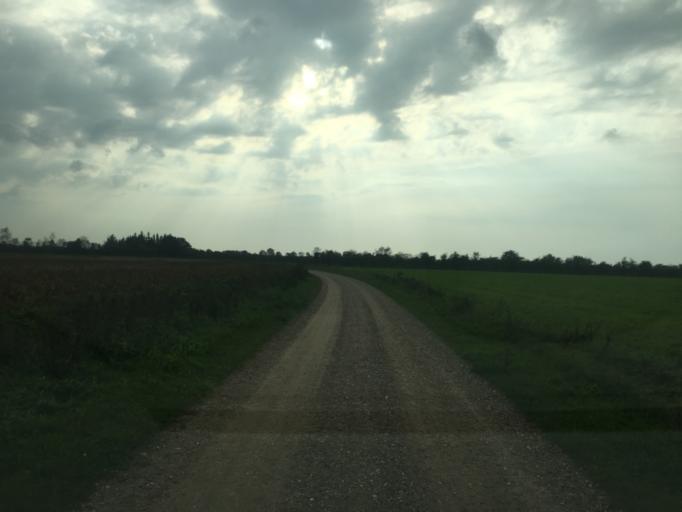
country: DK
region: South Denmark
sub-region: Tonder Kommune
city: Logumkloster
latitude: 54.9960
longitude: 9.0337
